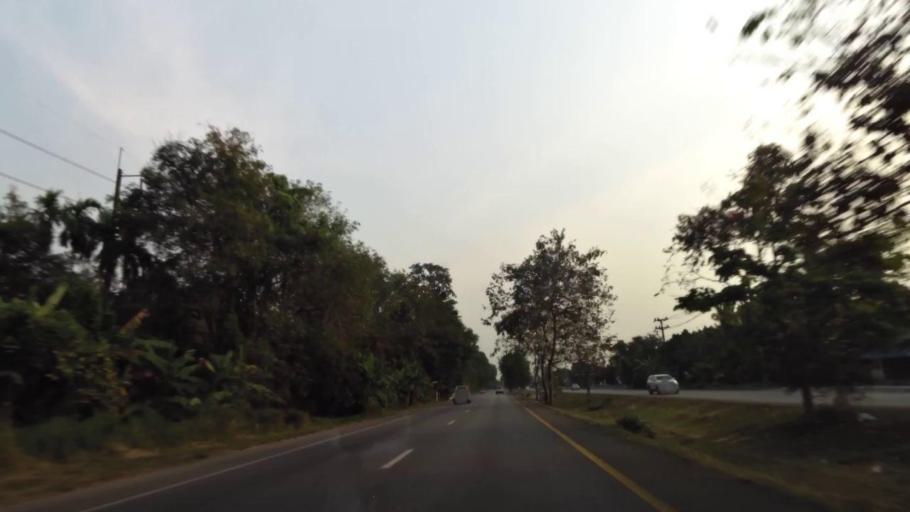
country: TH
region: Chanthaburi
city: Khlung
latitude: 12.4920
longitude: 102.1736
